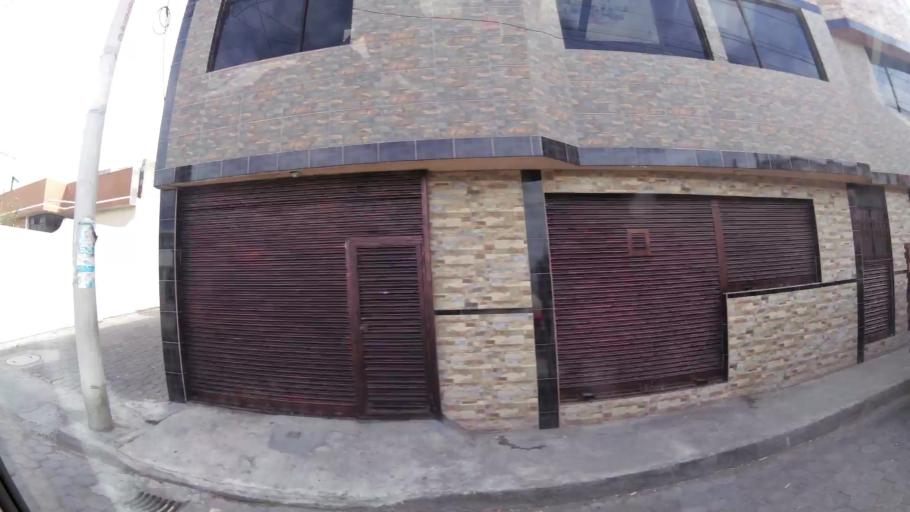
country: EC
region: Cotopaxi
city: Latacunga
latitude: -0.9279
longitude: -78.6078
